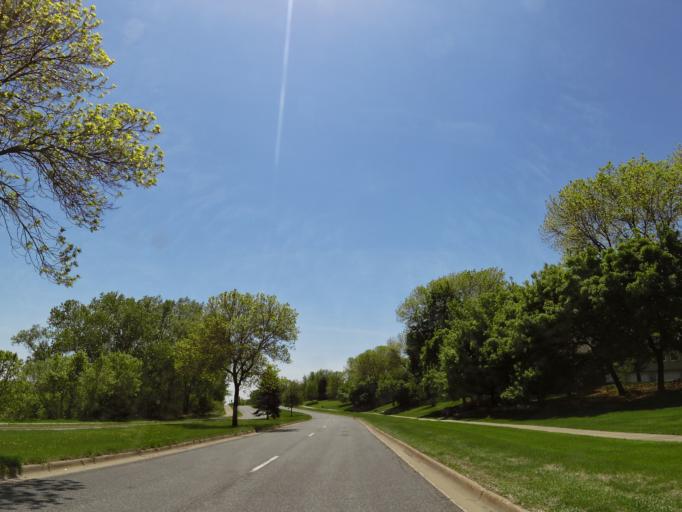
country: US
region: Minnesota
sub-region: Scott County
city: Savage
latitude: 44.8278
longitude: -93.3935
